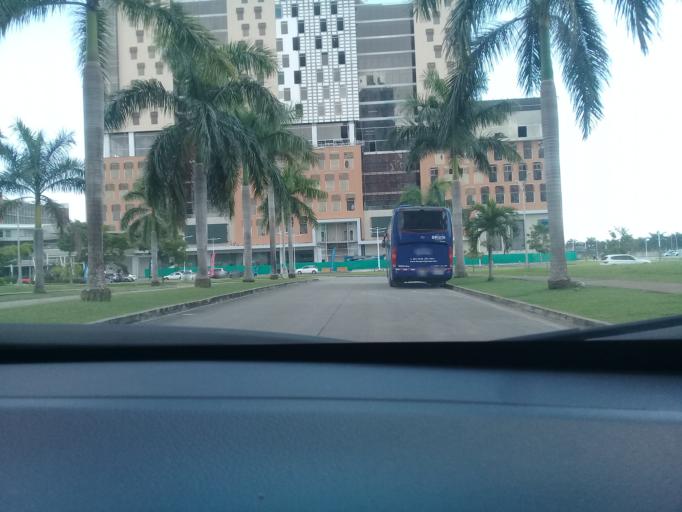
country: PA
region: Panama
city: San Miguelito
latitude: 9.0129
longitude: -79.4662
